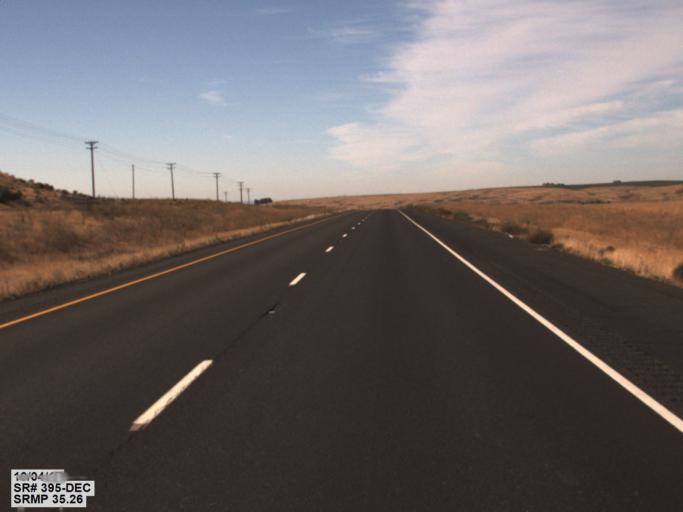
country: US
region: Washington
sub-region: Franklin County
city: Pasco
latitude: 46.4218
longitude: -119.0364
